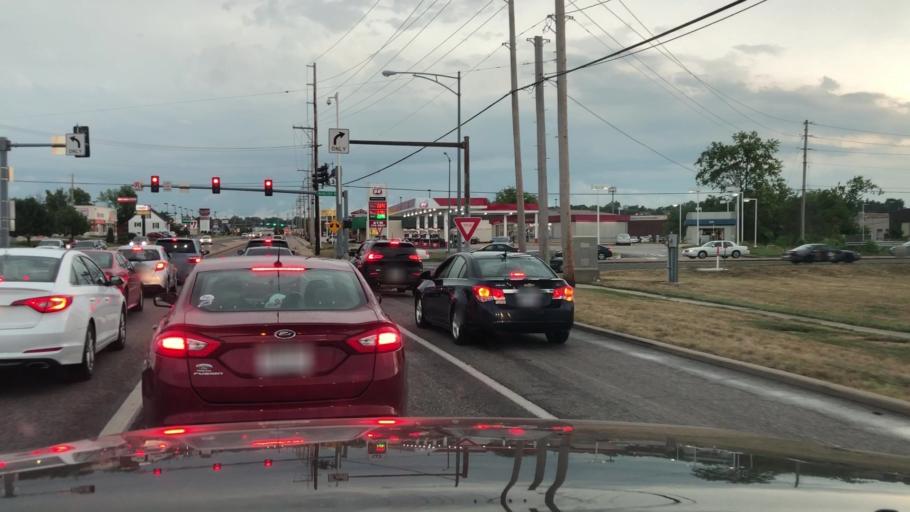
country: US
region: Missouri
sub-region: Saint Louis County
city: Bridgeton
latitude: 38.7515
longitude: -90.4268
